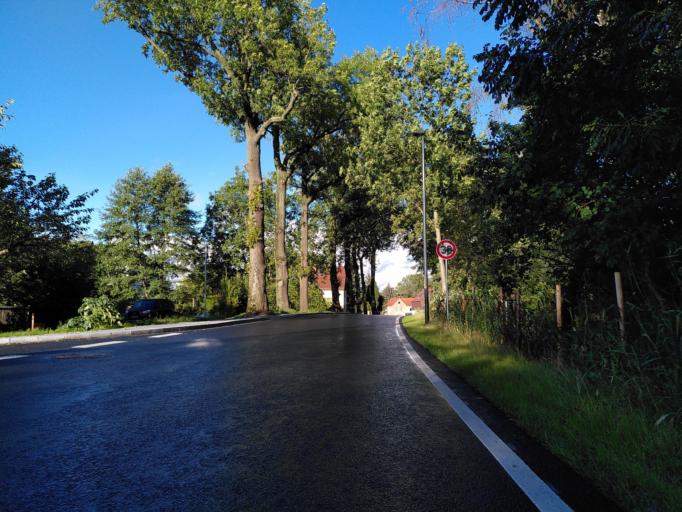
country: DE
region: Saxony
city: Radeberg
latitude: 51.0359
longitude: 13.9130
